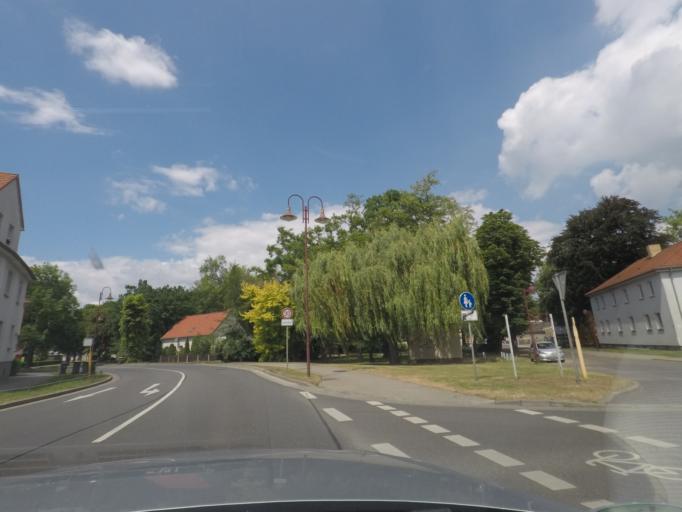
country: DE
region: Saxony
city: Markranstadt
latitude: 51.2983
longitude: 12.2237
